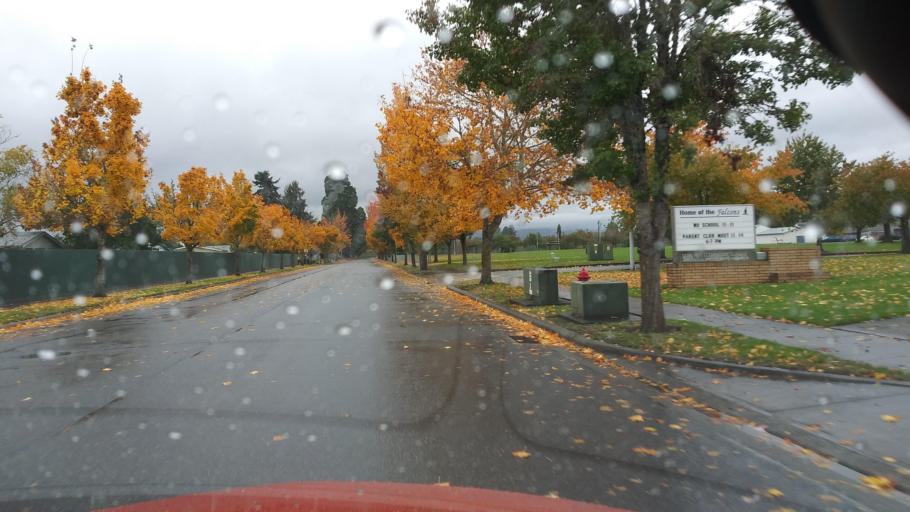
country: US
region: Oregon
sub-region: Washington County
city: Cornelius
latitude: 45.5139
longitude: -123.0723
